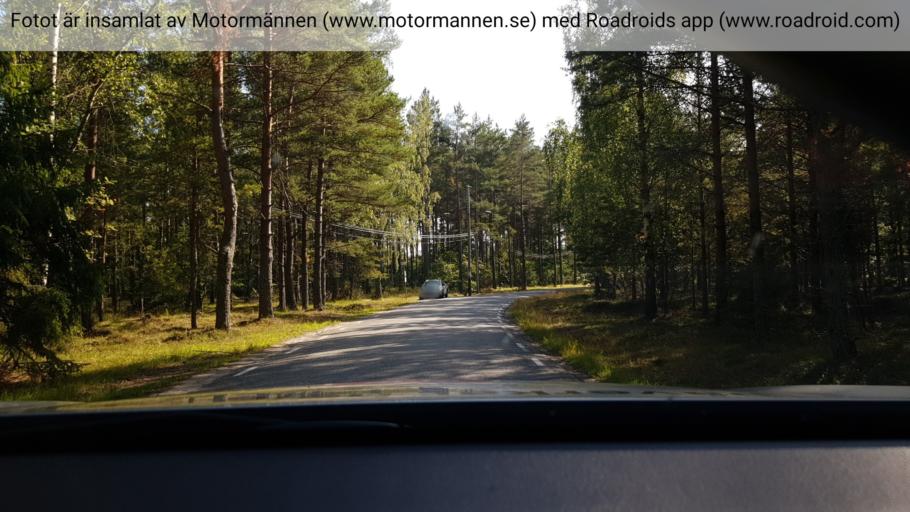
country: SE
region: Stockholm
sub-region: Nynashamns Kommun
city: Nynashamn
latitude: 58.8154
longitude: 17.8286
